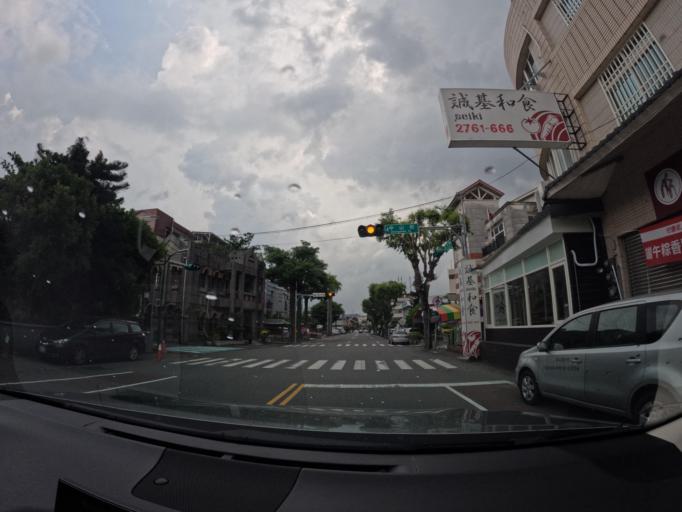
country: TW
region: Taiwan
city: Lugu
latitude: 23.8288
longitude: 120.7869
